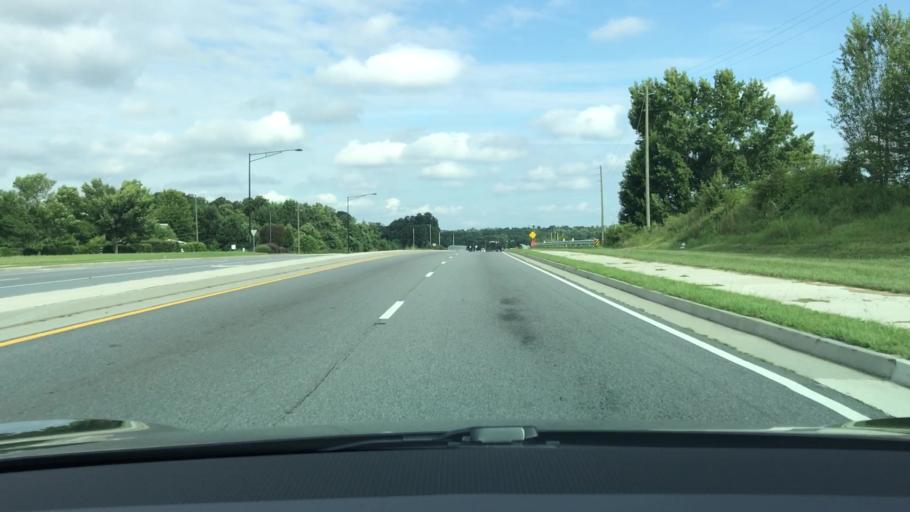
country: US
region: Georgia
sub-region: Gwinnett County
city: Buford
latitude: 34.1449
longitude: -83.9678
